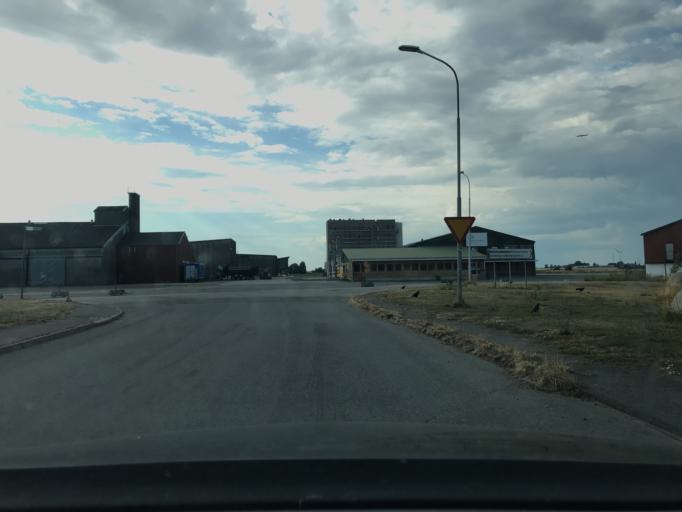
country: SE
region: Skane
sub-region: Tomelilla Kommun
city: Tomelilla
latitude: 55.5062
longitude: 14.1523
